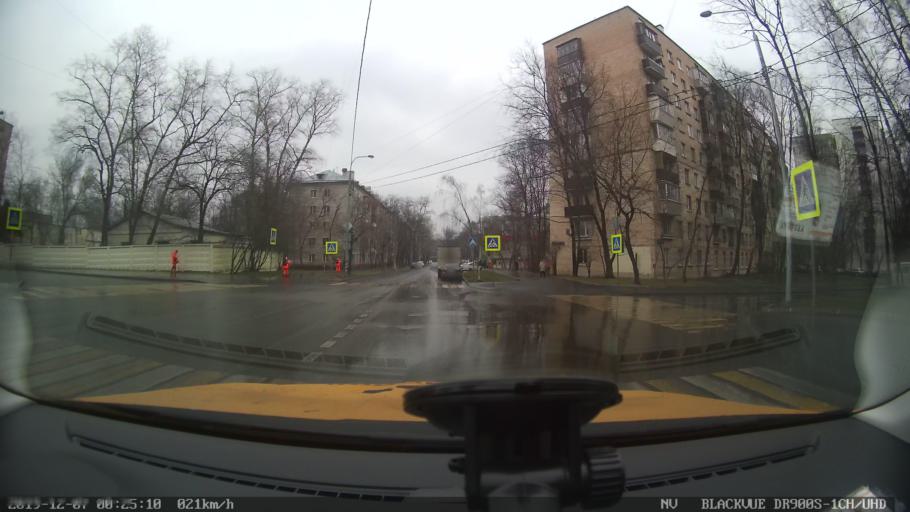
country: RU
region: Moscow
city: Rostokino
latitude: 55.8303
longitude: 37.6645
